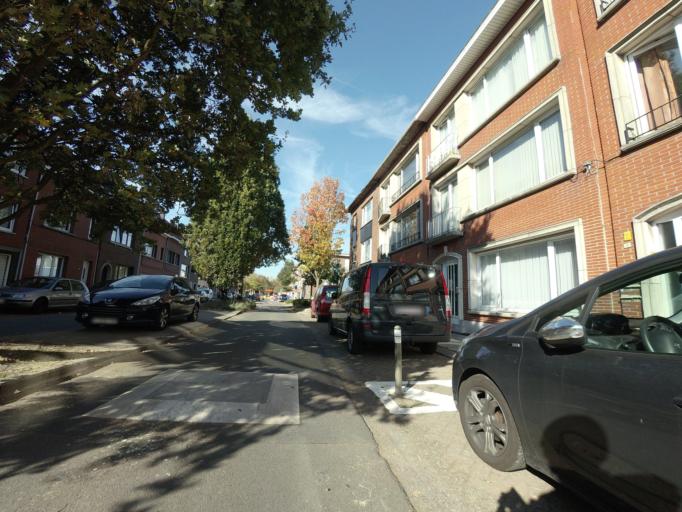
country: BE
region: Flanders
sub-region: Provincie Antwerpen
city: Borsbeek
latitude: 51.2212
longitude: 4.4826
